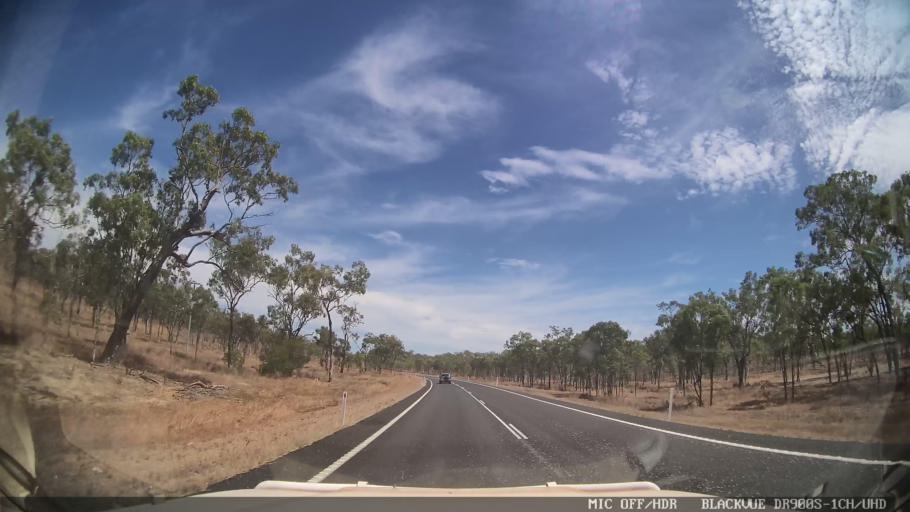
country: AU
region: Queensland
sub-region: Cook
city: Cooktown
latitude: -15.7592
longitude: 144.9951
